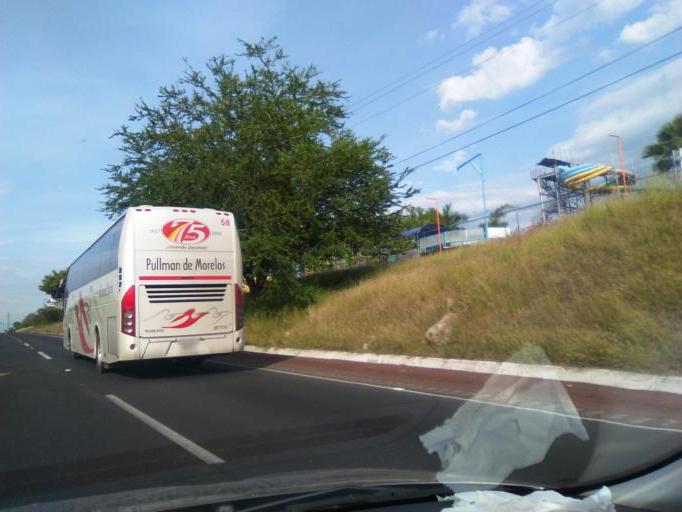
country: MX
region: Morelos
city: Alpuyeca
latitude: 18.7427
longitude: -99.2482
